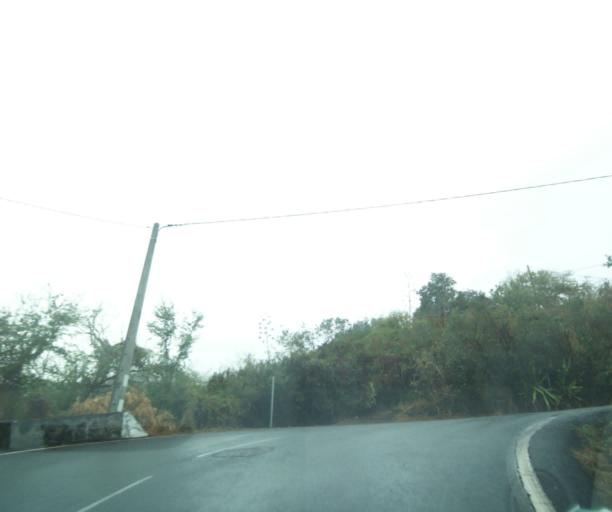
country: RE
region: Reunion
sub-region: Reunion
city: Saint-Paul
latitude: -21.0190
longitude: 55.2892
